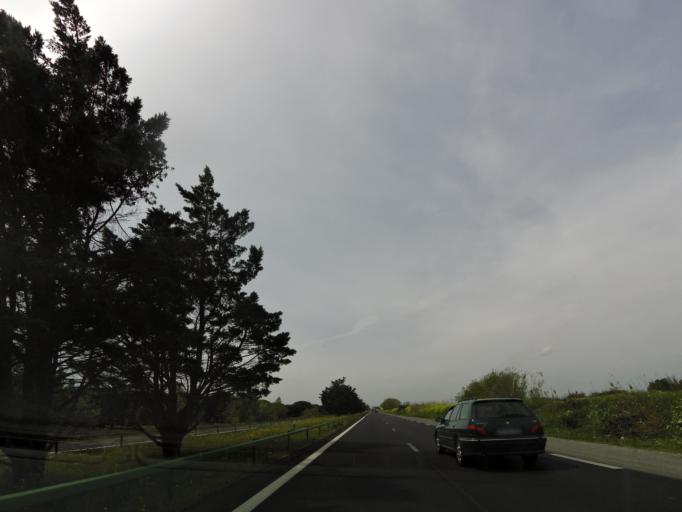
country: FR
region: Languedoc-Roussillon
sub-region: Departement de l'Herault
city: La Grande-Motte
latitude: 43.5641
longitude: 4.0477
